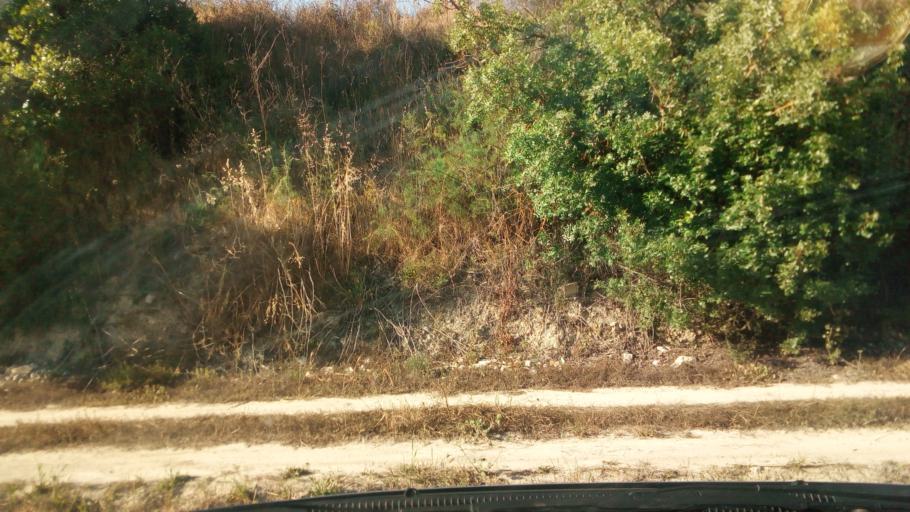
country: CY
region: Pafos
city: Tala
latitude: 34.8774
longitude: 32.4784
